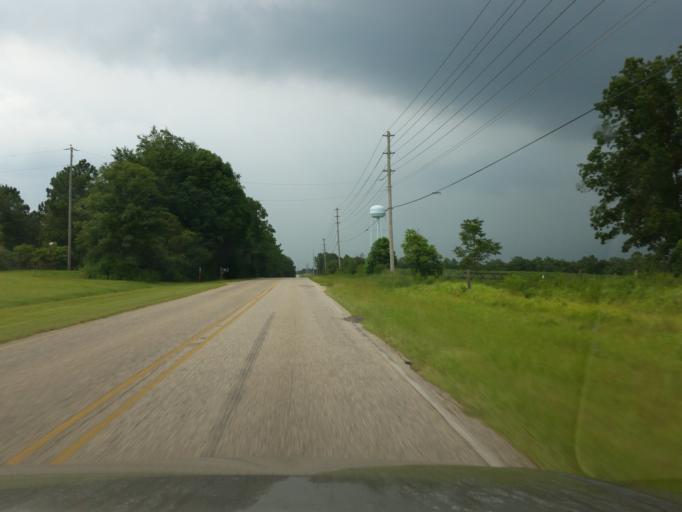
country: US
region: Alabama
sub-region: Baldwin County
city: Robertsdale
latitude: 30.5526
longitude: -87.5816
